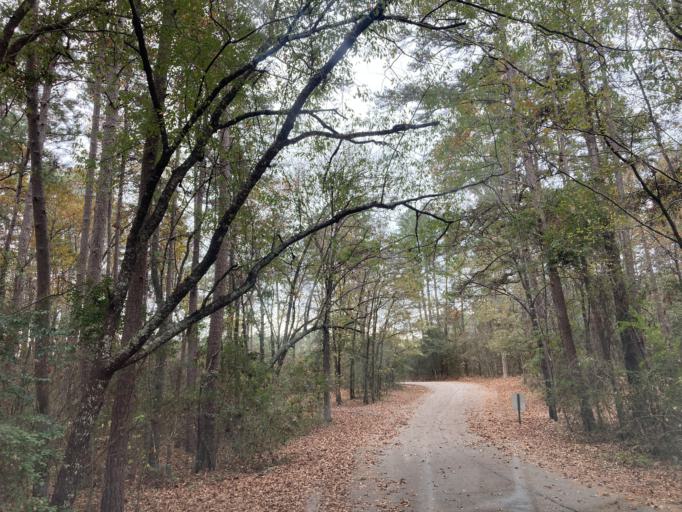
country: US
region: Mississippi
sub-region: Lamar County
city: Lumberton
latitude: 31.0824
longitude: -89.4967
